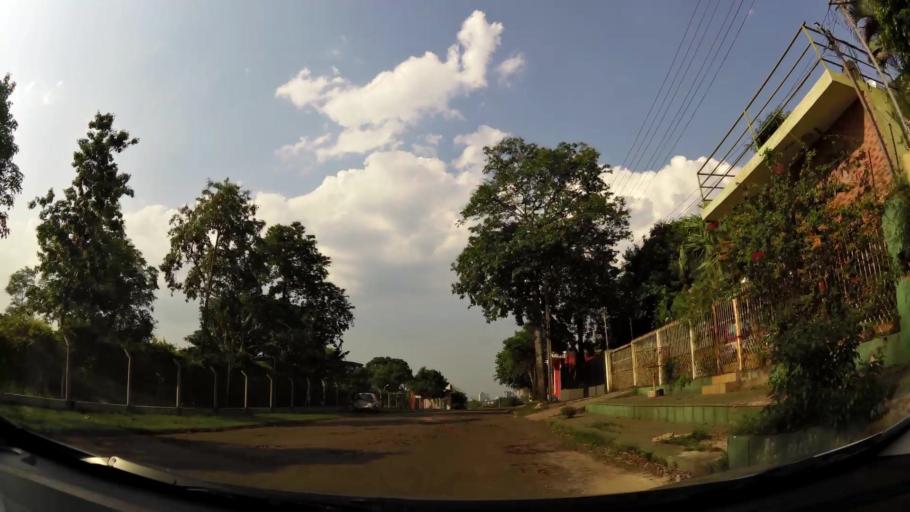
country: PY
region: Alto Parana
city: Presidente Franco
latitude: -25.5281
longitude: -54.6276
